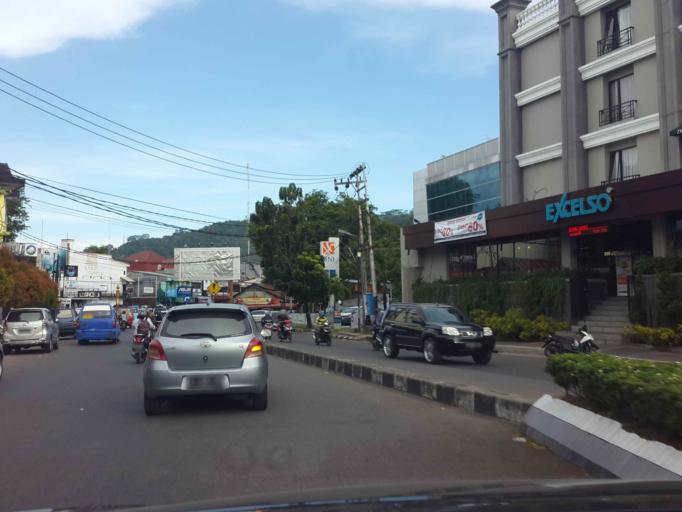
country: ID
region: West Sumatra
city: Padang
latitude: -0.9541
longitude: 100.3593
